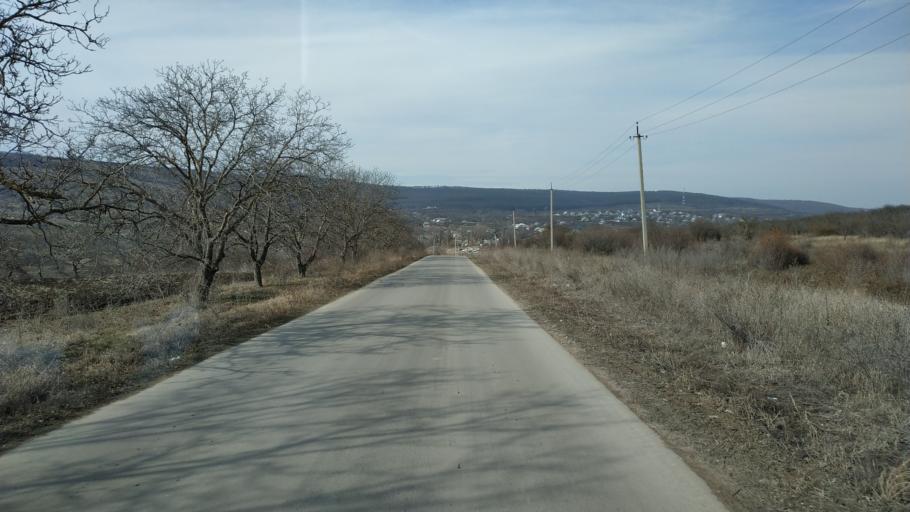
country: MD
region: Nisporeni
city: Nisporeni
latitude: 47.1467
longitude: 28.1182
